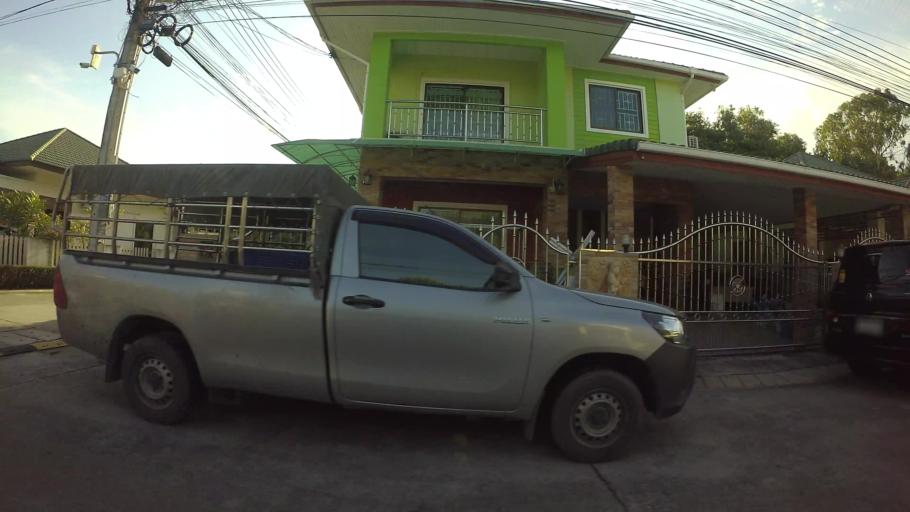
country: TH
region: Rayong
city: Rayong
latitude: 12.6836
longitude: 101.2909
